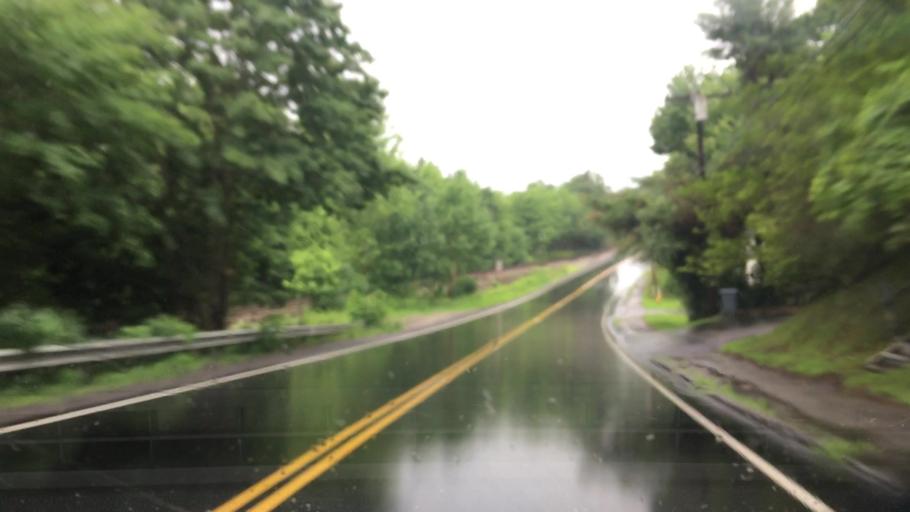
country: US
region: Maine
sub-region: Kennebec County
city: Randolph
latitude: 44.2246
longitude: -69.7660
